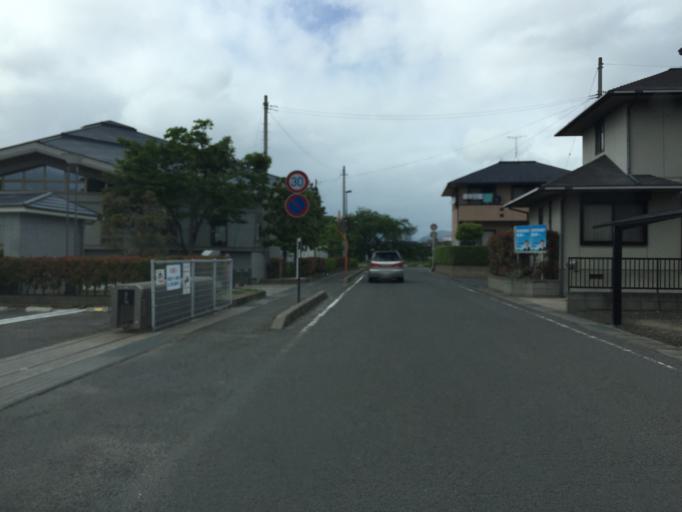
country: JP
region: Fukushima
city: Fukushima-shi
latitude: 37.7803
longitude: 140.4577
